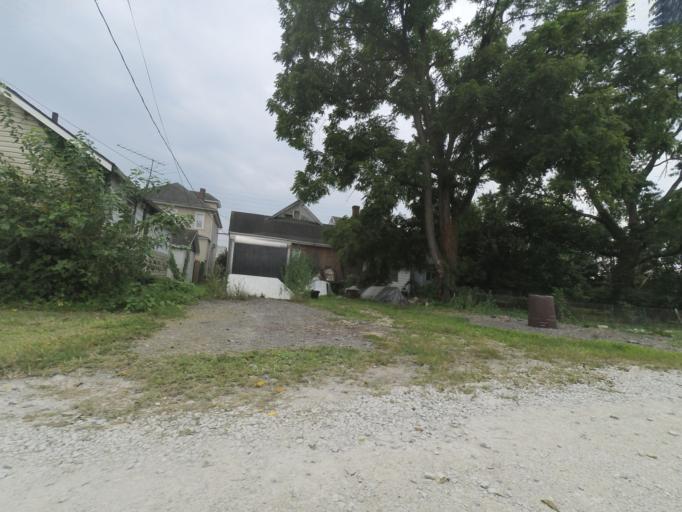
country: US
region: West Virginia
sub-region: Cabell County
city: Huntington
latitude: 38.4195
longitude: -82.4200
